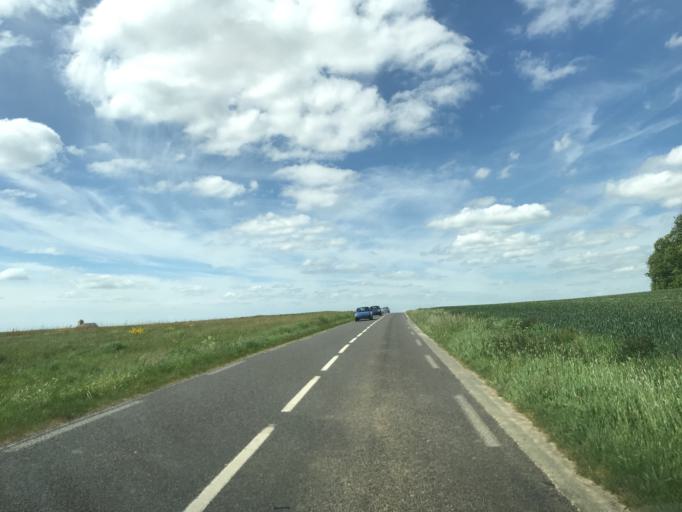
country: FR
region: Haute-Normandie
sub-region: Departement de l'Eure
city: Nassandres
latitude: 49.1571
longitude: 0.8084
